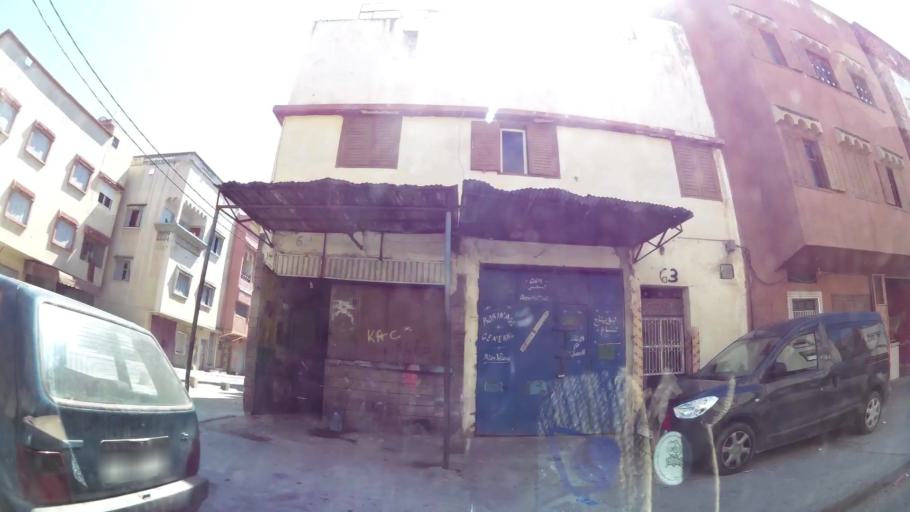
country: MA
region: Gharb-Chrarda-Beni Hssen
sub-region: Kenitra Province
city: Kenitra
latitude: 34.2416
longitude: -6.5534
